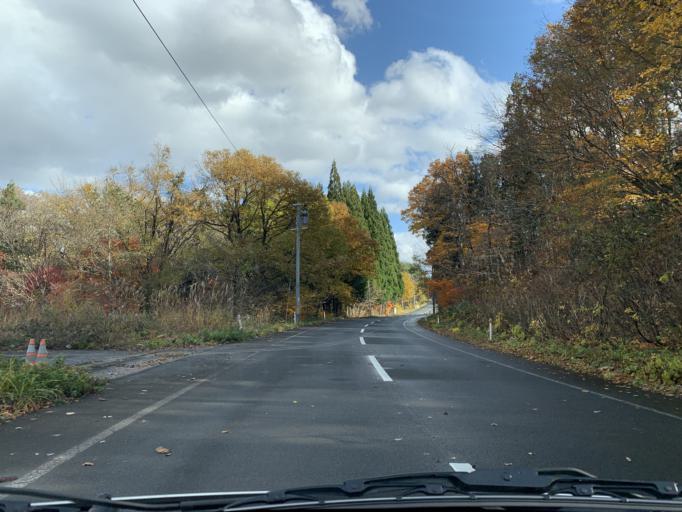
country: JP
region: Iwate
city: Mizusawa
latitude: 39.1136
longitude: 140.9577
